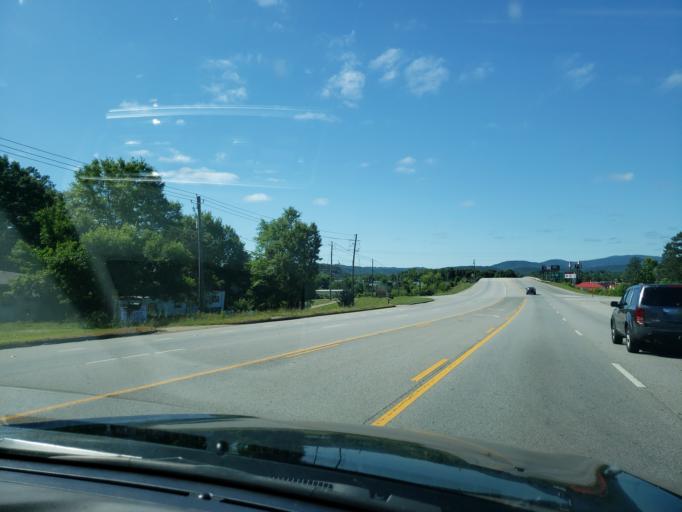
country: US
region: Alabama
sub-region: Calhoun County
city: Oxford
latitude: 33.6188
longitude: -85.7862
